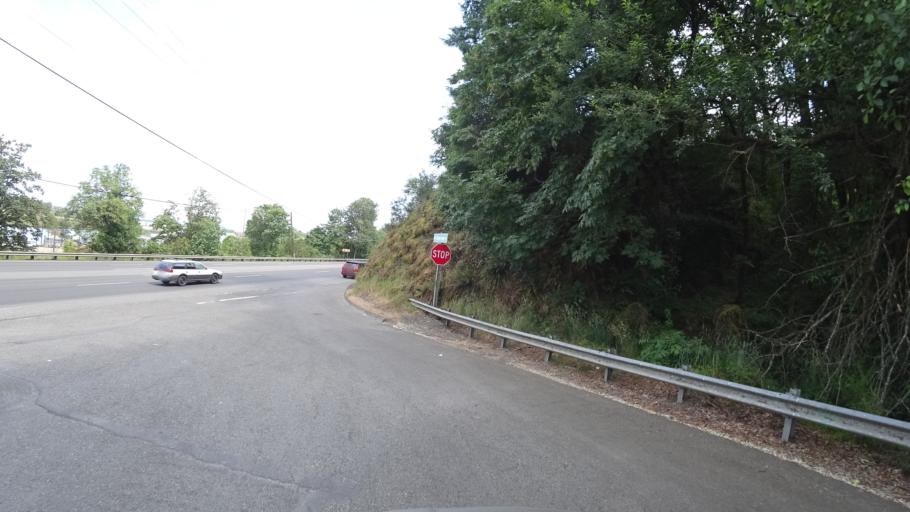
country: US
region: Oregon
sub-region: Washington County
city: Bethany
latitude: 45.6208
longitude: -122.8117
